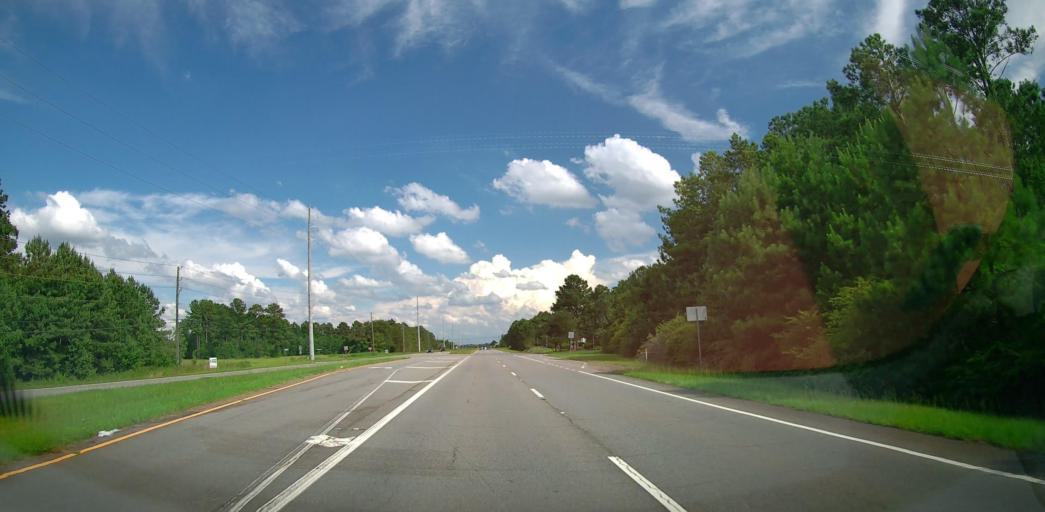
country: US
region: Georgia
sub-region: Houston County
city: Perry
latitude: 32.4816
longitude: -83.7117
